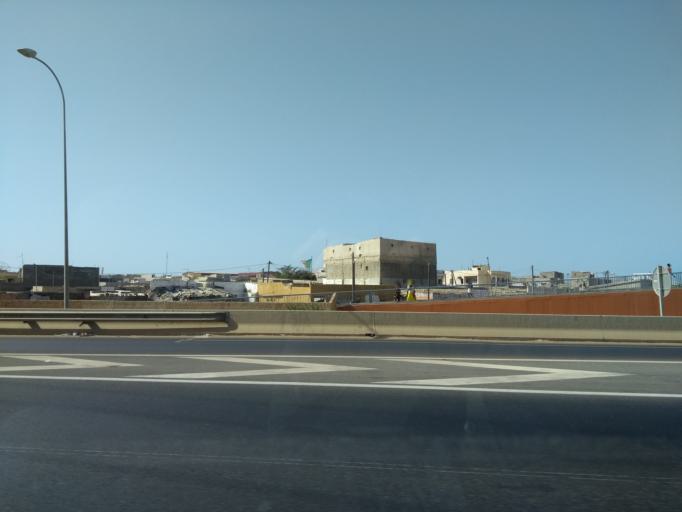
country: SN
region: Dakar
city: Pikine
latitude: 14.7482
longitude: -17.3817
